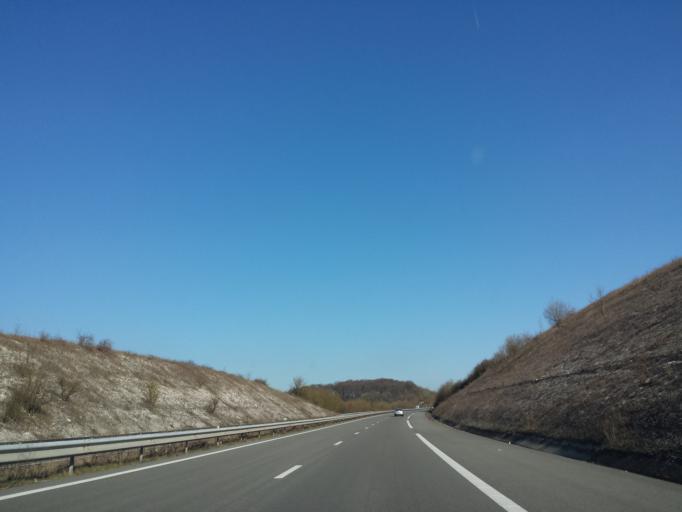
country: FR
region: Picardie
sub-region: Departement de la Somme
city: Conty
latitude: 49.6748
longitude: 2.2107
